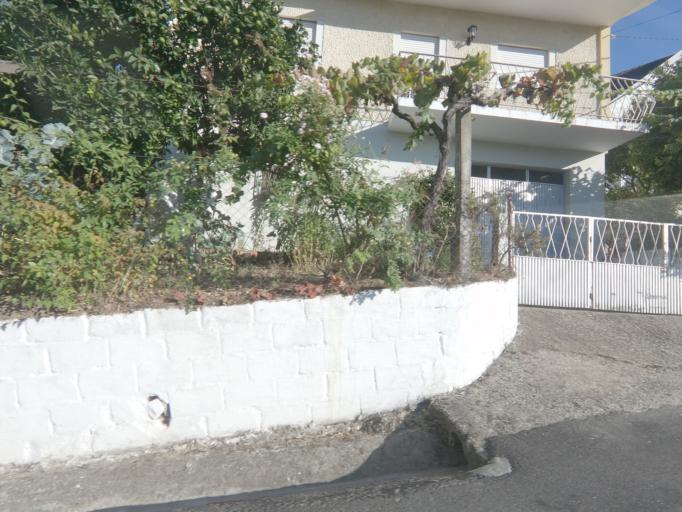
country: PT
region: Vila Real
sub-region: Santa Marta de Penaguiao
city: Santa Marta de Penaguiao
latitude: 41.1970
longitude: -7.7727
